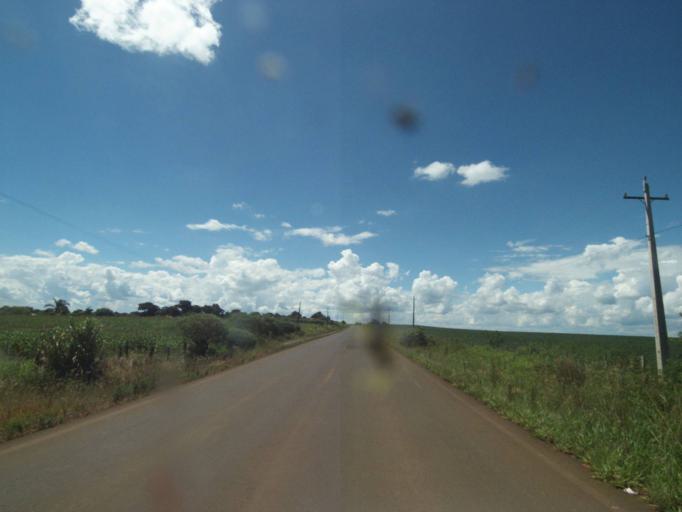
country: BR
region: Parana
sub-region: Pinhao
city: Pinhao
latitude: -25.8182
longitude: -52.0421
